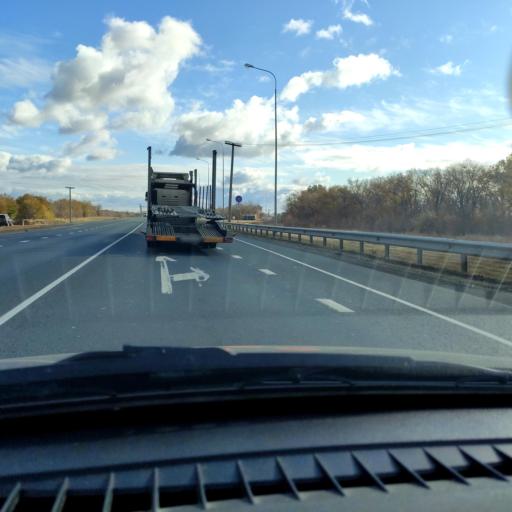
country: RU
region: Samara
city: Varlamovo
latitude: 53.1918
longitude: 48.3412
